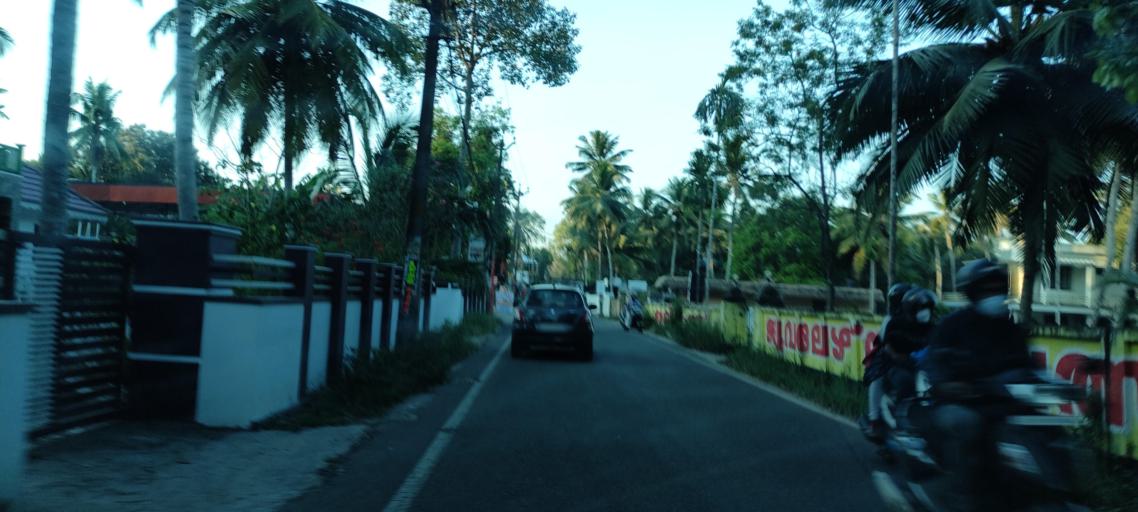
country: IN
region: Kerala
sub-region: Alappuzha
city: Kayankulam
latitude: 9.2351
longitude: 76.4560
